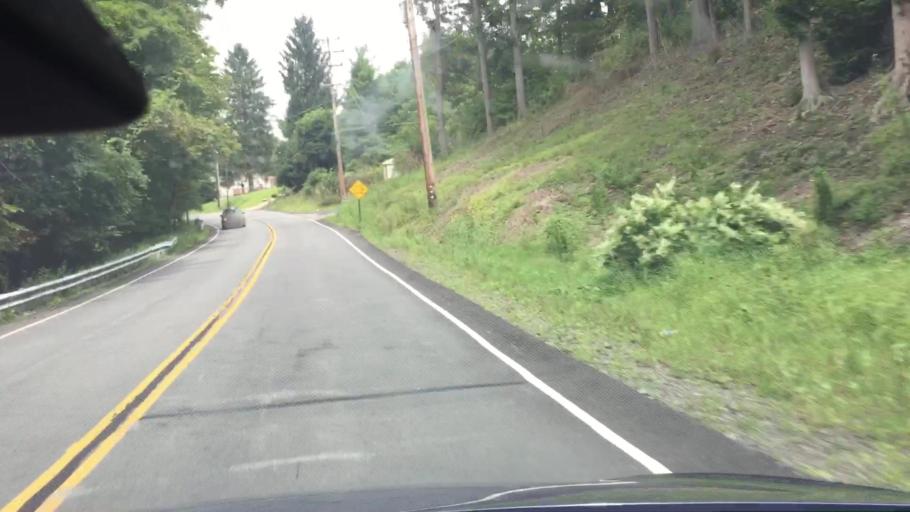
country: US
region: Pennsylvania
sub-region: Allegheny County
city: Monroeville
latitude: 40.4298
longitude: -79.7762
